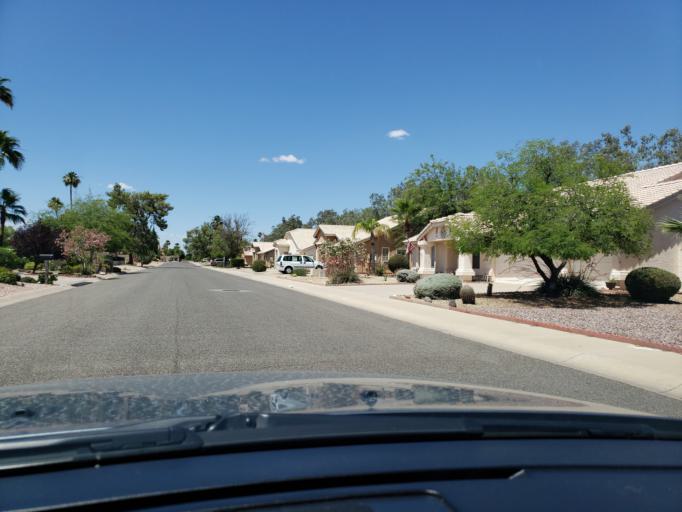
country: US
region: Arizona
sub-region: Maricopa County
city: Paradise Valley
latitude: 33.6088
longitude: -112.0176
